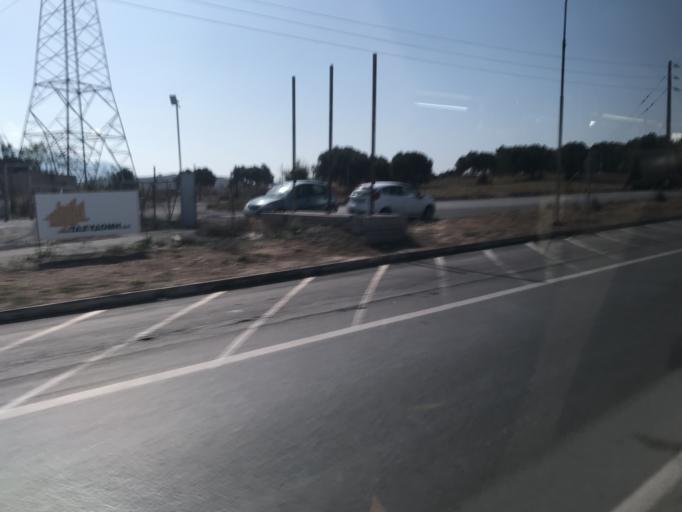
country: GR
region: Crete
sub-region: Nomos Irakleiou
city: Gazi
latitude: 35.3077
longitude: 25.0893
